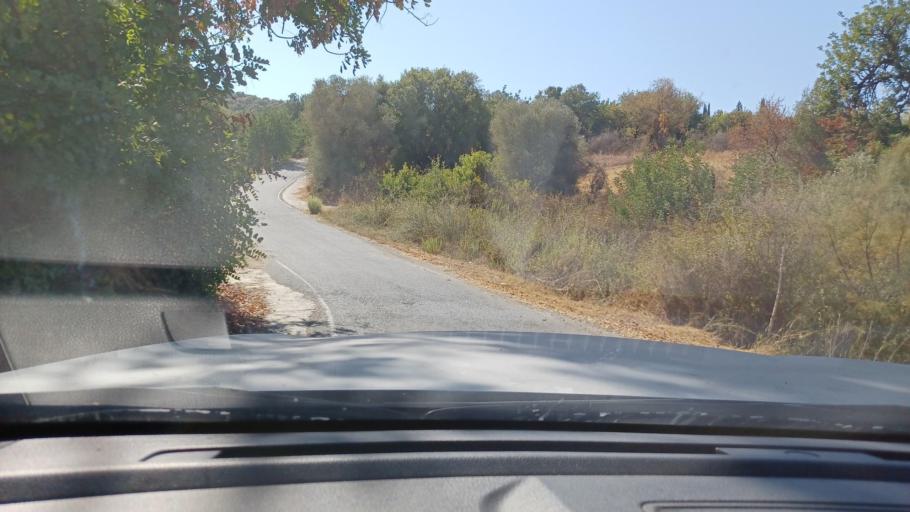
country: CY
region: Pafos
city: Polis
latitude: 34.9987
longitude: 32.4978
